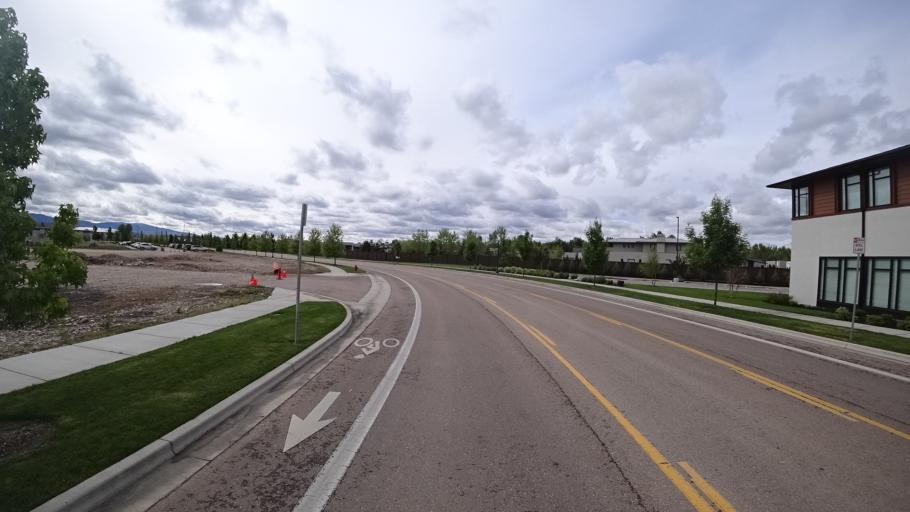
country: US
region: Idaho
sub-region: Ada County
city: Eagle
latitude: 43.6862
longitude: -116.3337
